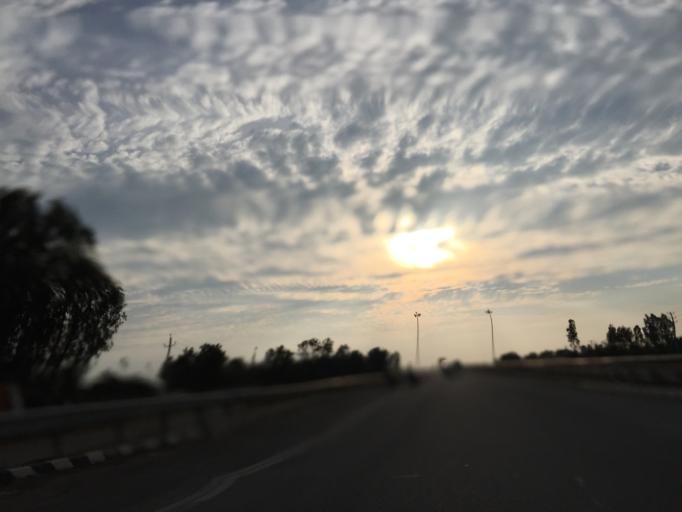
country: IN
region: Karnataka
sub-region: Kolar
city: Kolar
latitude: 13.1426
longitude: 78.2338
